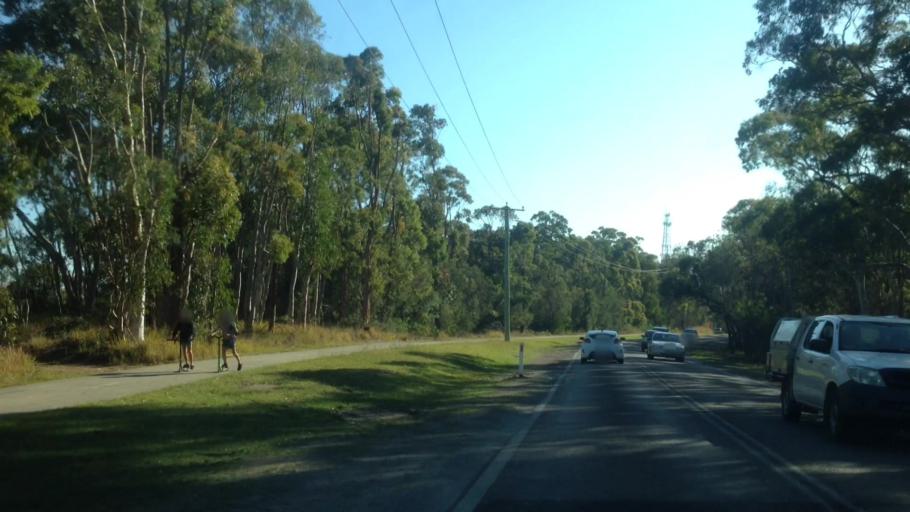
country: AU
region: New South Wales
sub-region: Lake Macquarie Shire
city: Dora Creek
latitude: -33.1123
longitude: 151.5219
